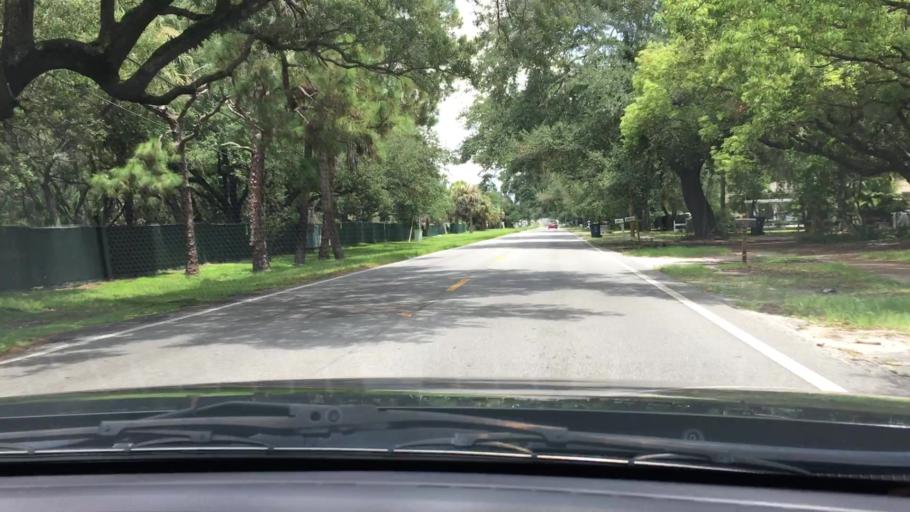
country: US
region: Florida
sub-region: Hillsborough County
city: Tampa
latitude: 27.9011
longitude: -82.5267
